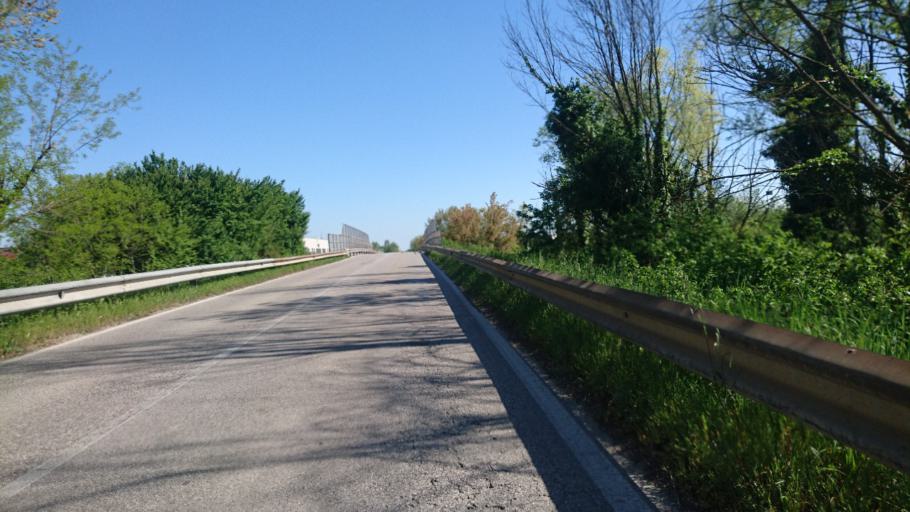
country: IT
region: Veneto
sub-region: Provincia di Venezia
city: Dese
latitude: 45.5407
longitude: 12.2875
